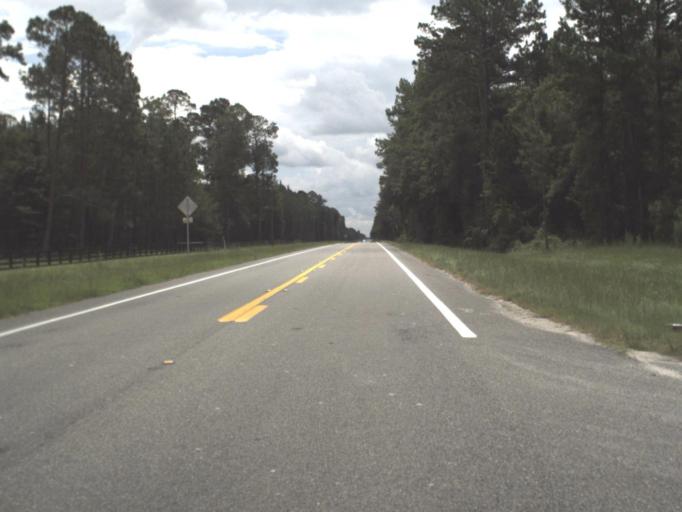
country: US
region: Florida
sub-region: Union County
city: Lake Butler
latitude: 30.0545
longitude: -82.4122
